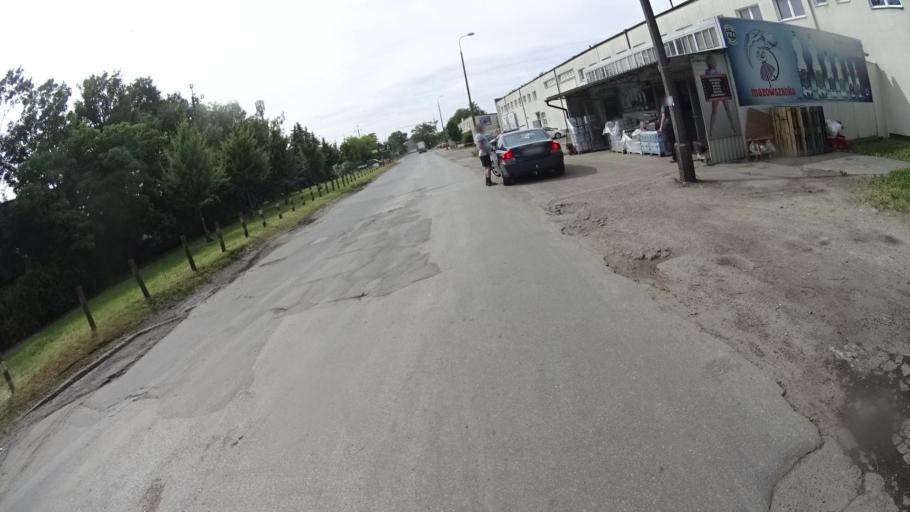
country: PL
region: Masovian Voivodeship
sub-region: Warszawa
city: Wlochy
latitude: 52.1901
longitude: 20.9390
